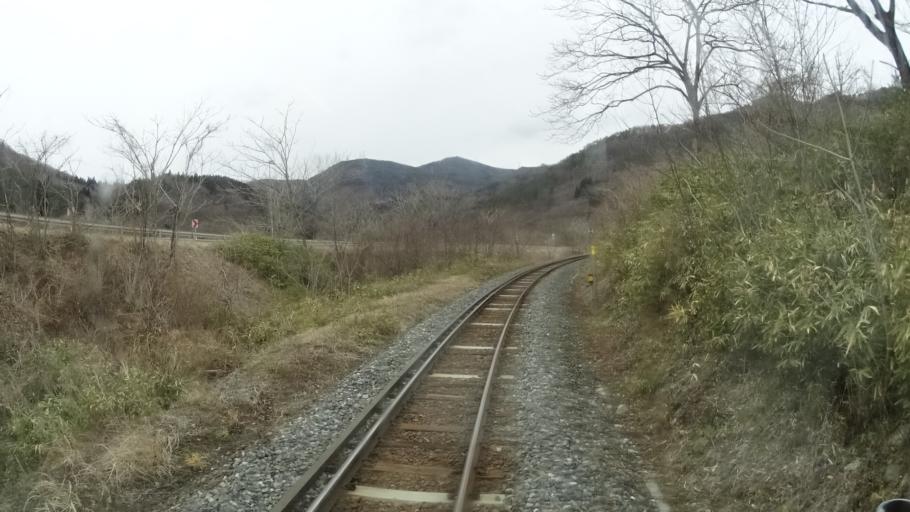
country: JP
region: Iwate
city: Hanamaki
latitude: 39.3560
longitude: 141.3092
